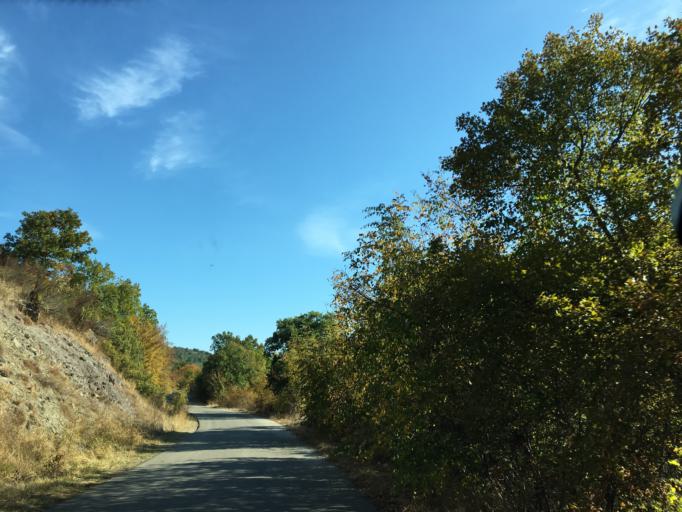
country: BG
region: Khaskovo
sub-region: Obshtina Ivaylovgrad
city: Ivaylovgrad
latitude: 41.4058
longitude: 26.1246
